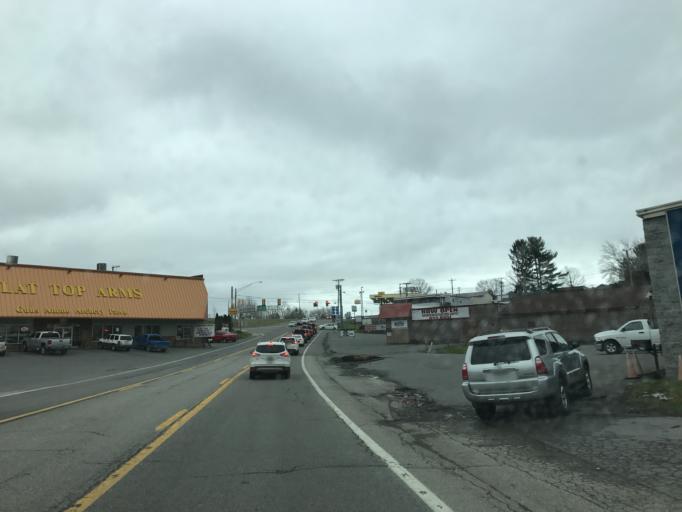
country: US
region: West Virginia
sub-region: Raleigh County
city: Beckley
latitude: 37.7752
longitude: -81.1622
